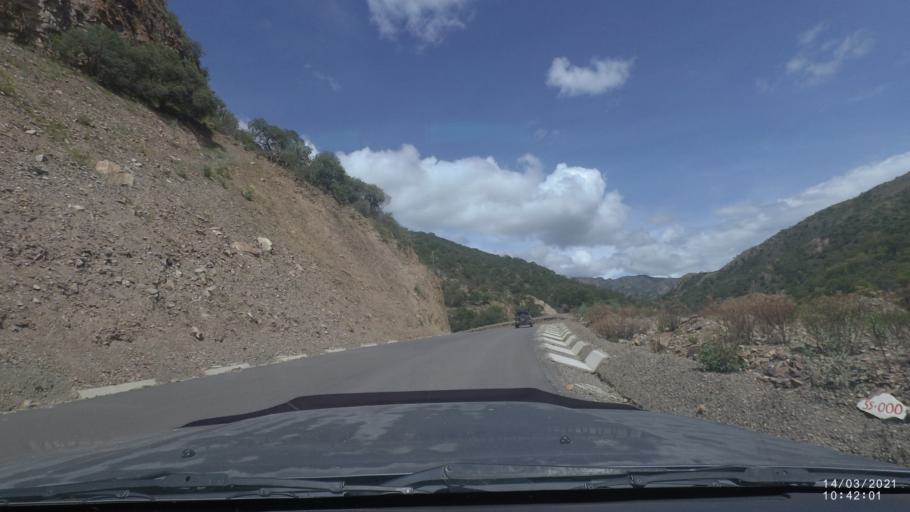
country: BO
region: Cochabamba
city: Tarata
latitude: -17.8786
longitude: -65.9156
